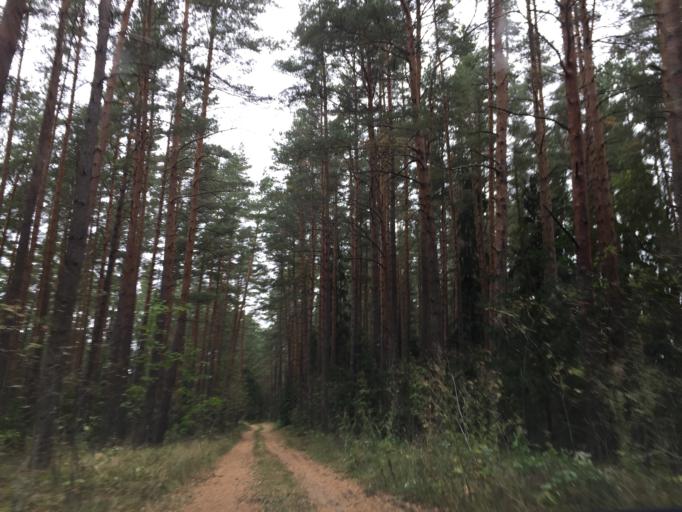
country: LV
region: Salacgrivas
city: Salacgriva
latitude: 57.7041
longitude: 24.3557
